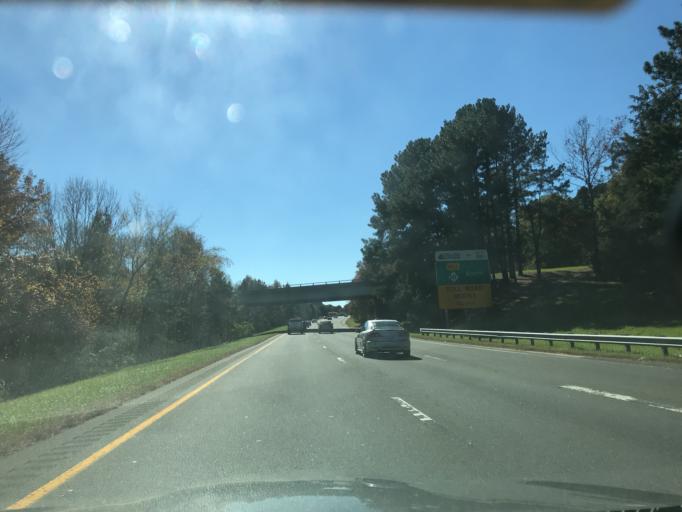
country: US
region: North Carolina
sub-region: Durham County
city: Durham
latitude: 35.9126
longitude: -78.8647
